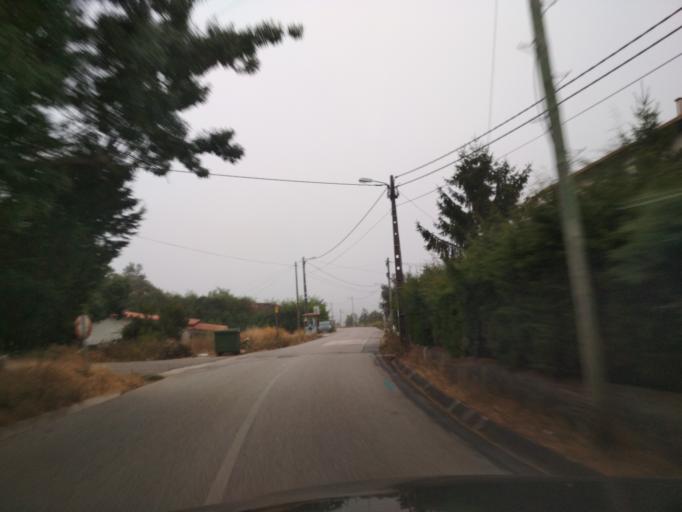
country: PT
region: Coimbra
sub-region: Coimbra
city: Coimbra
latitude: 40.1861
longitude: -8.4391
